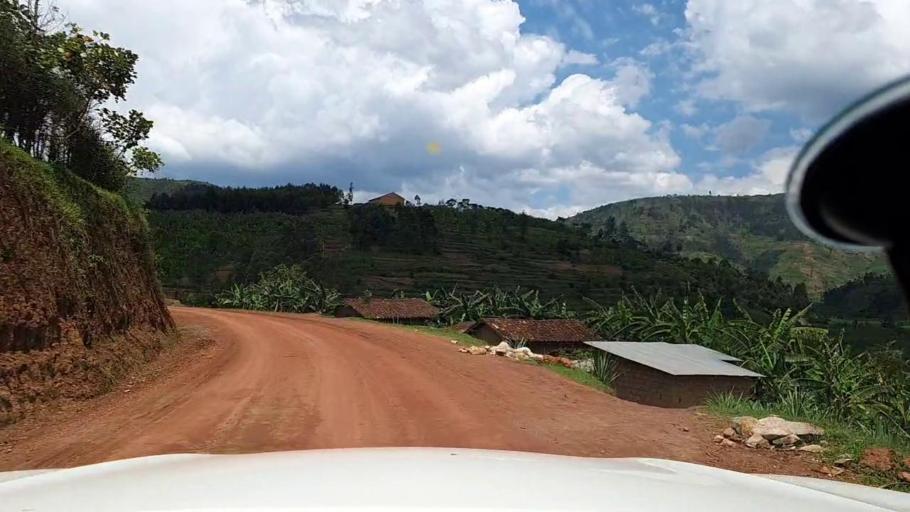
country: RW
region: Northern Province
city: Musanze
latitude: -1.6926
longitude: 29.8200
